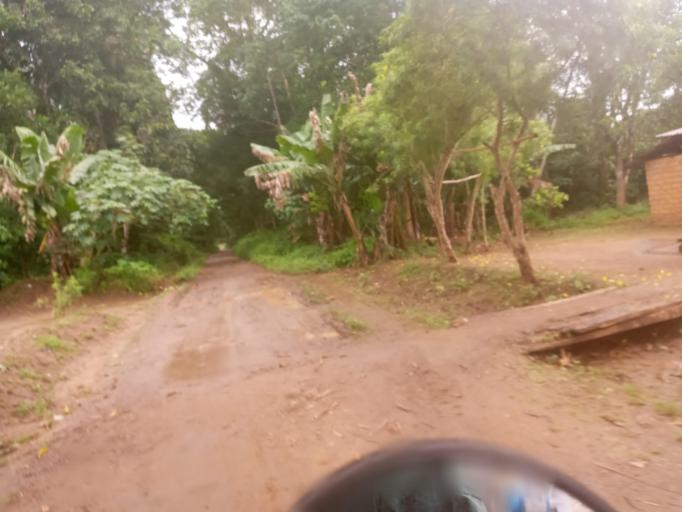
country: SL
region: Northern Province
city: Bumbuna
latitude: 8.9430
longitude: -11.7500
